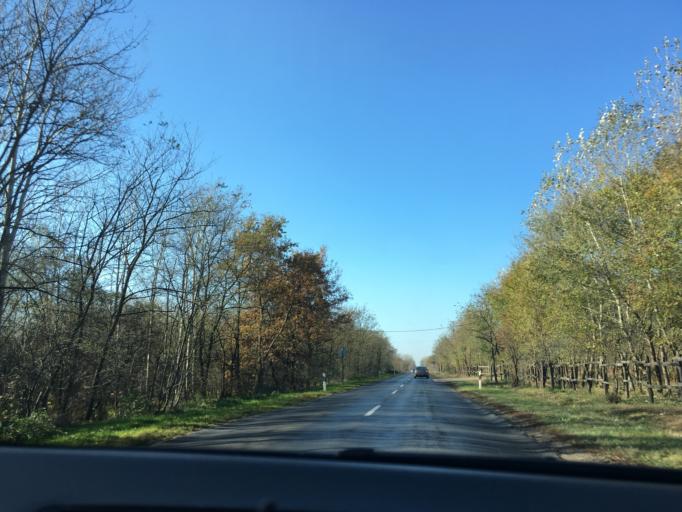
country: HU
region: Hajdu-Bihar
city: Hajdusamson
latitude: 47.5268
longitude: 21.7912
